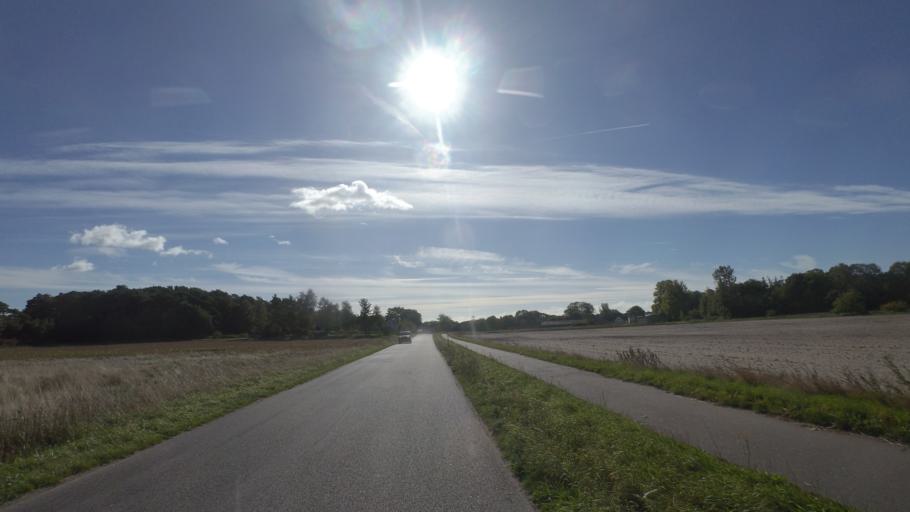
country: DK
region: Capital Region
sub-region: Bornholm Kommune
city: Akirkeby
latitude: 55.0114
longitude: 14.9915
